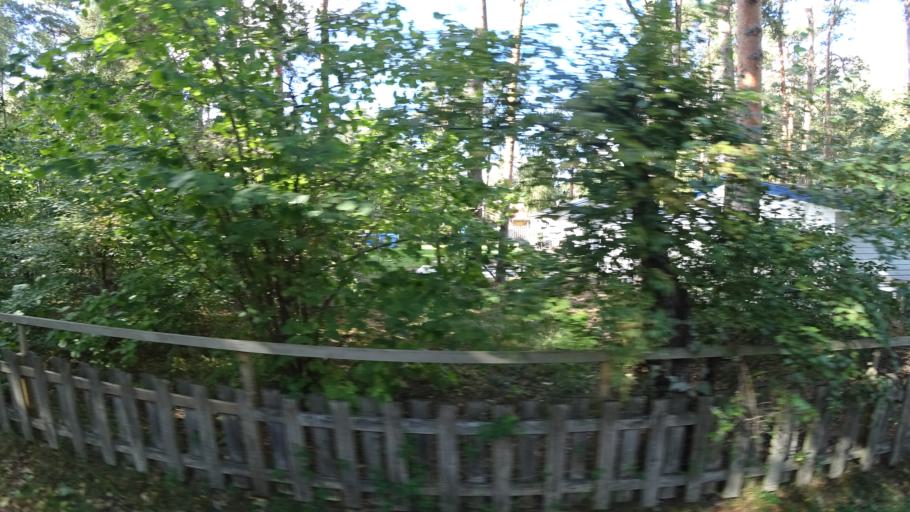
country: SE
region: Skane
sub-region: Kavlinge Kommun
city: Hofterup
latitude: 55.7568
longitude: 12.9837
